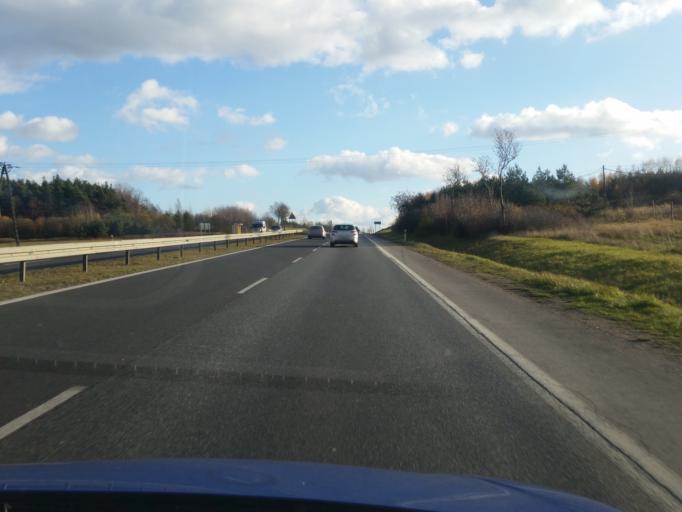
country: PL
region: Silesian Voivodeship
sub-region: Powiat myszkowski
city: Kozieglowy
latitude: 50.5643
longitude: 19.1723
